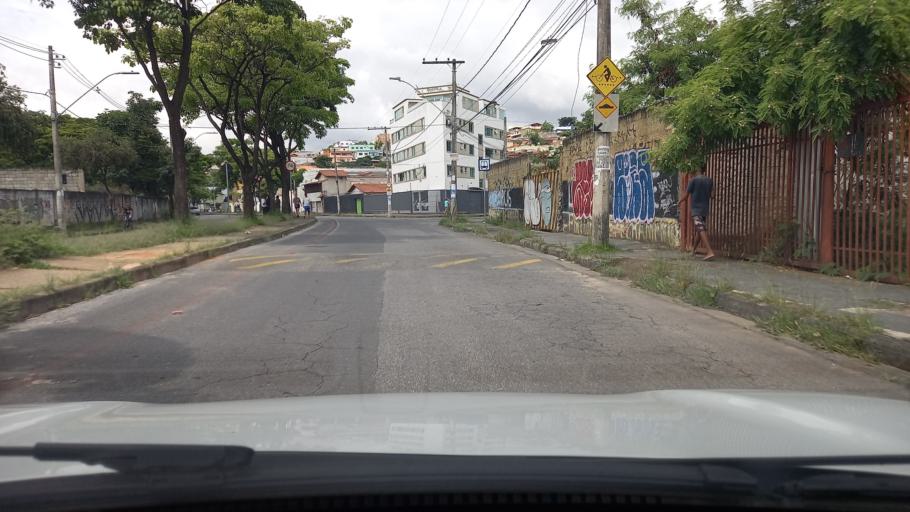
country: BR
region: Minas Gerais
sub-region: Contagem
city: Contagem
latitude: -19.8971
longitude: -44.0158
